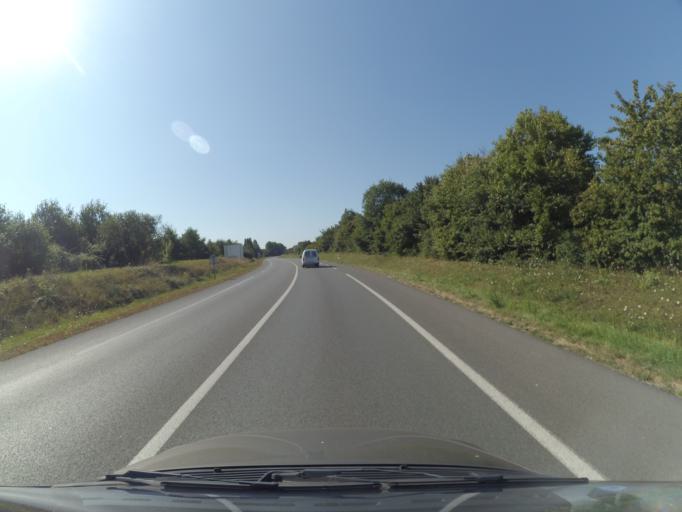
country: FR
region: Pays de la Loire
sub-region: Departement de la Vendee
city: Bouffere
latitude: 46.9719
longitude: -1.3525
